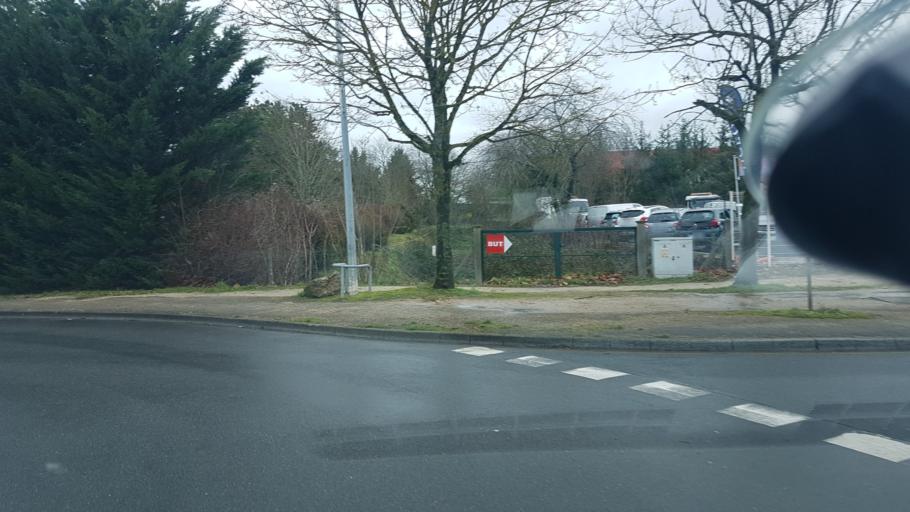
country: FR
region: Ile-de-France
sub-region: Departement de Seine-et-Marne
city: Nemours
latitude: 48.2659
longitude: 2.7149
